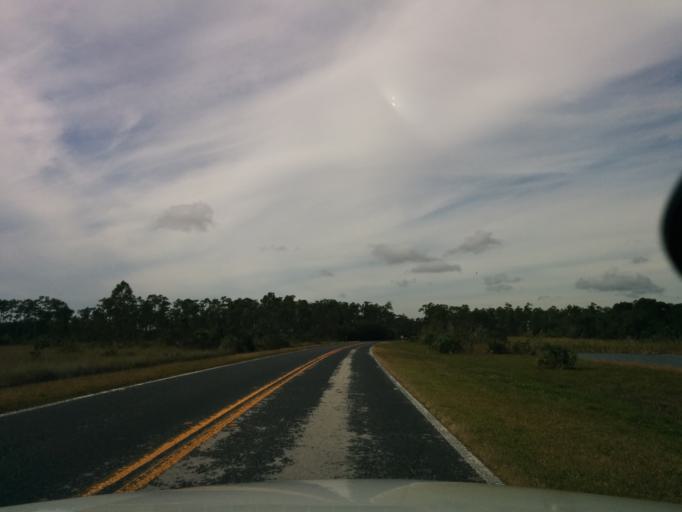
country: US
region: Florida
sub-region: Miami-Dade County
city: Florida City
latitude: 25.3945
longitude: -80.5820
